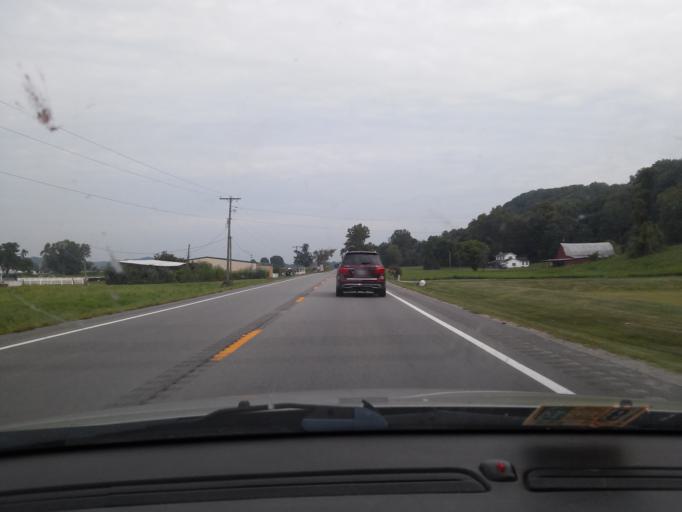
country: US
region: West Virginia
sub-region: Putnam County
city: Buffalo
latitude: 38.7076
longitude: -81.9671
